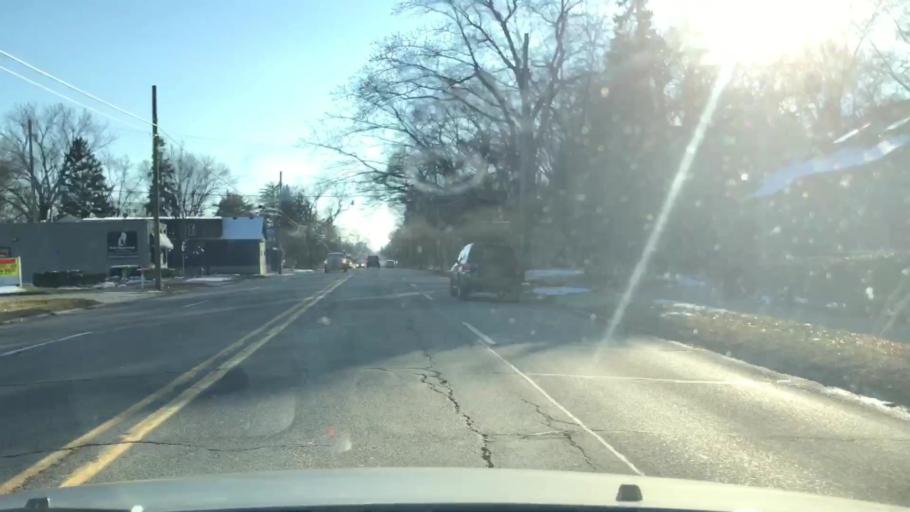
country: US
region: Michigan
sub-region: Oakland County
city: Clawson
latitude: 42.5121
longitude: -83.1412
